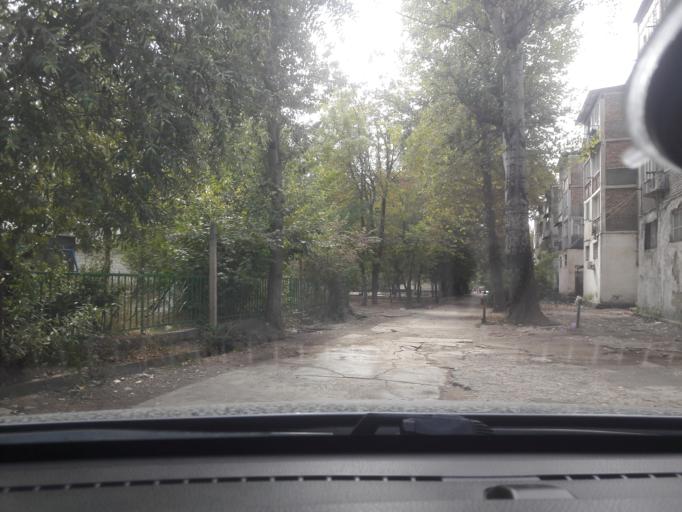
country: TJ
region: Dushanbe
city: Dushanbe
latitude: 38.5871
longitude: 68.7499
